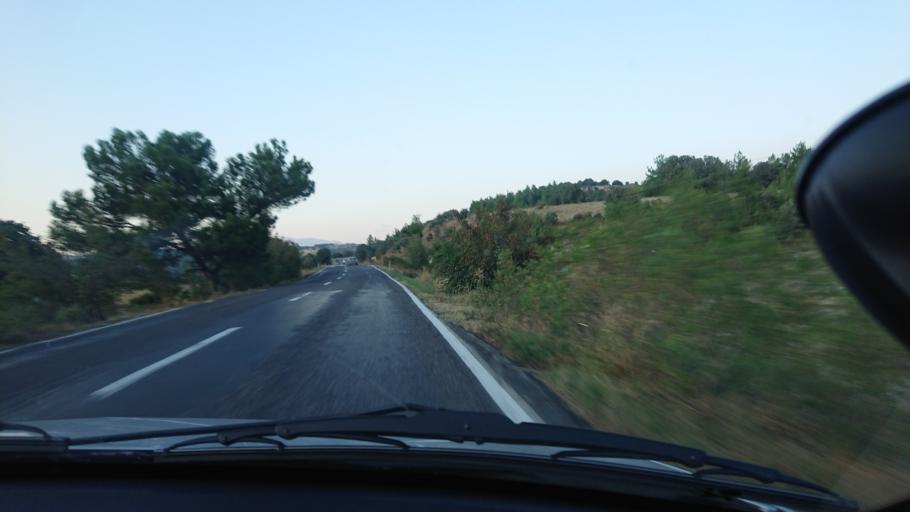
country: TR
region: Usak
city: Gure
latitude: 38.8009
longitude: 29.2360
